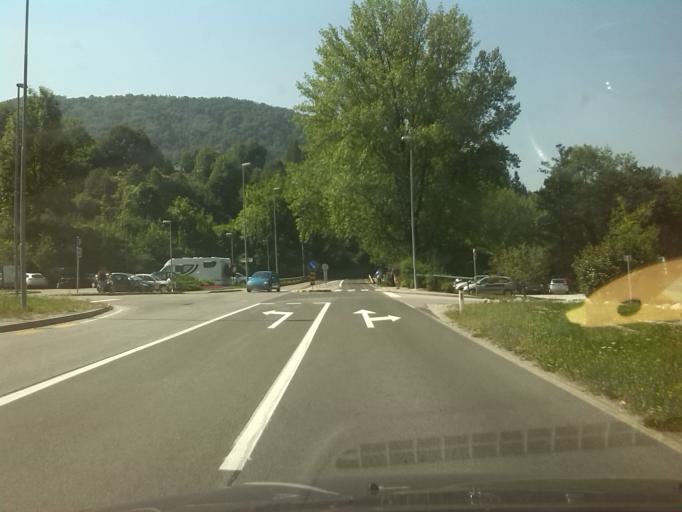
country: SI
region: Tolmin
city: Tolmin
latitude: 46.1561
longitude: 13.7475
